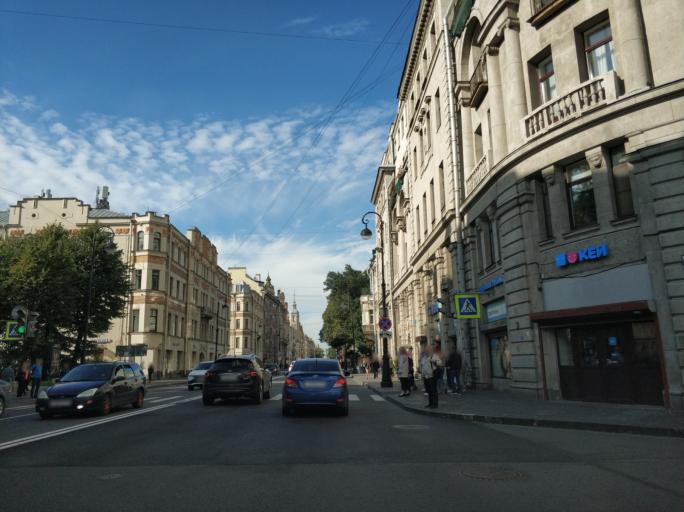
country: RU
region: St.-Petersburg
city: Petrogradka
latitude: 59.9581
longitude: 30.3192
